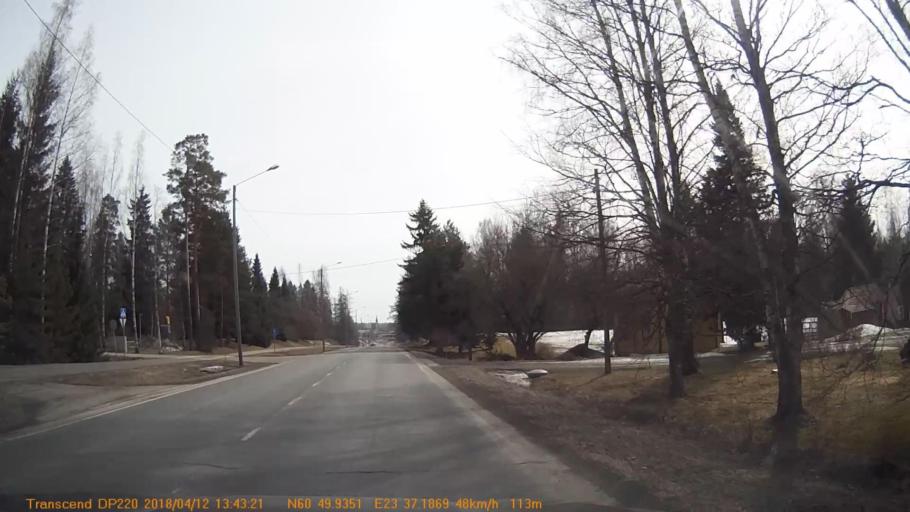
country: FI
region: Haeme
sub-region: Forssa
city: Forssa
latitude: 60.8319
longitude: 23.6200
